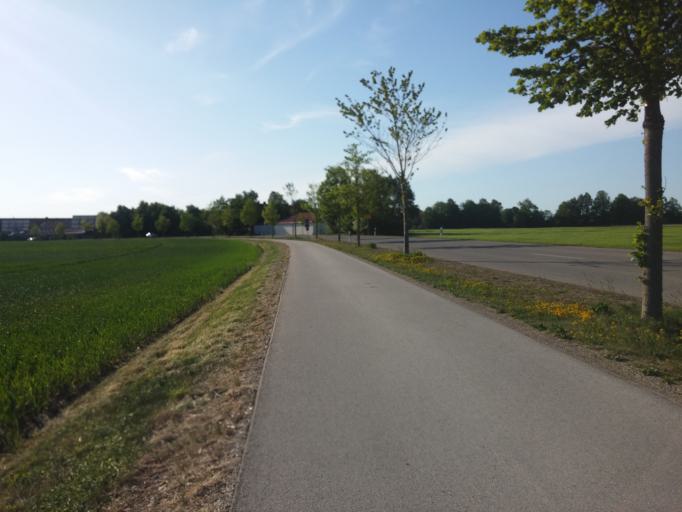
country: DE
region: Bavaria
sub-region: Upper Bavaria
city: Haar
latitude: 48.1252
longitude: 11.7460
